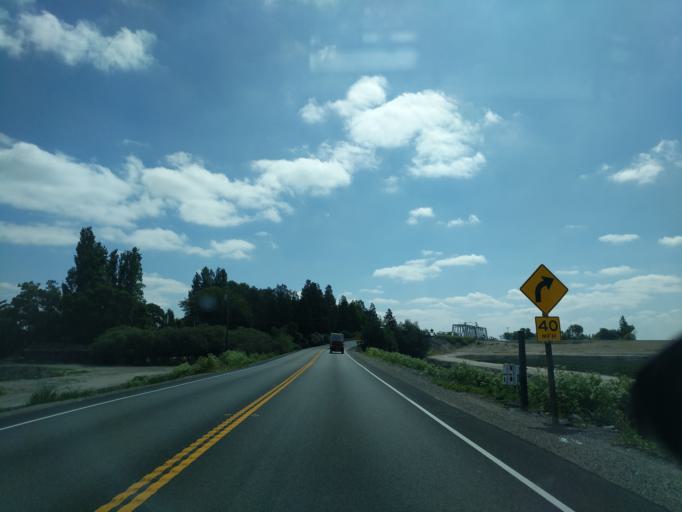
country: US
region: California
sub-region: Contra Costa County
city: Discovery Bay
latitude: 37.8916
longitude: -121.4934
